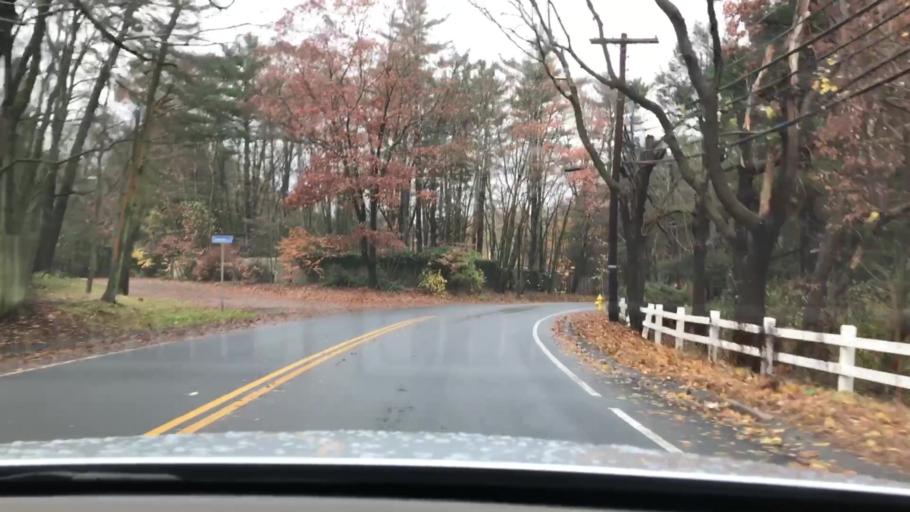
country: US
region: Massachusetts
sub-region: Norfolk County
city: Dedham
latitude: 42.2537
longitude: -71.1877
